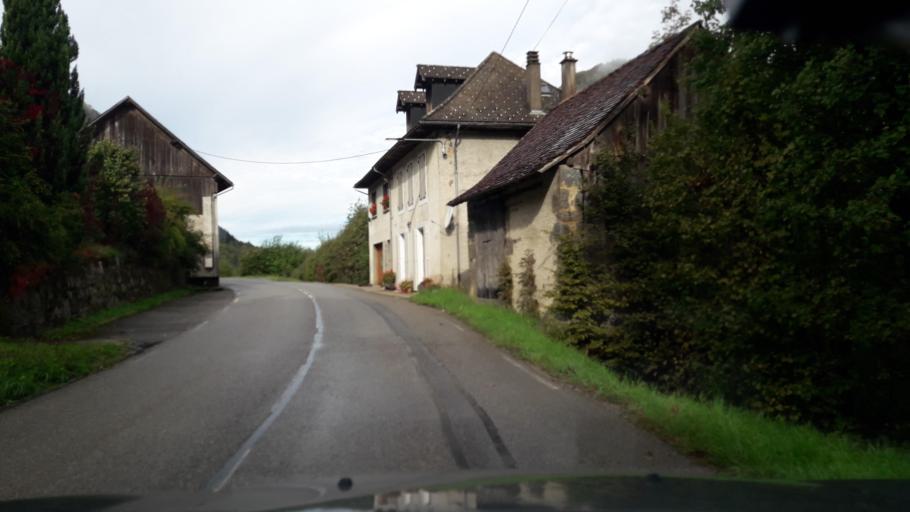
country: FR
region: Rhone-Alpes
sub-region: Departement de la Savoie
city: Les Echelles
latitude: 45.4163
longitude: 5.8517
